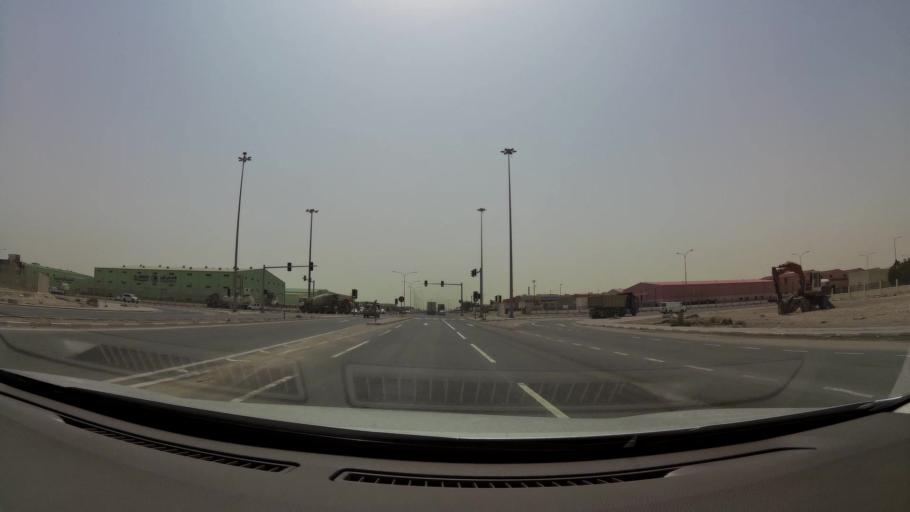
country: QA
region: Al Wakrah
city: Al Wukayr
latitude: 25.1599
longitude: 51.4082
